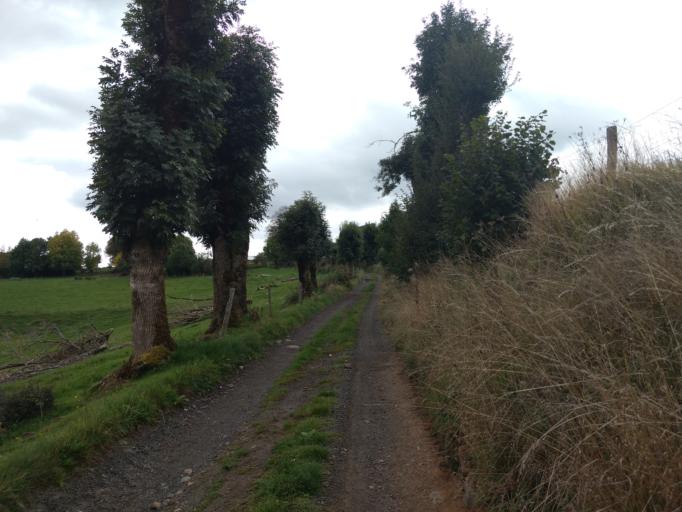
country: FR
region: Auvergne
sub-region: Departement du Cantal
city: Chaudes-Aigues
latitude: 44.8452
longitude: 2.9864
